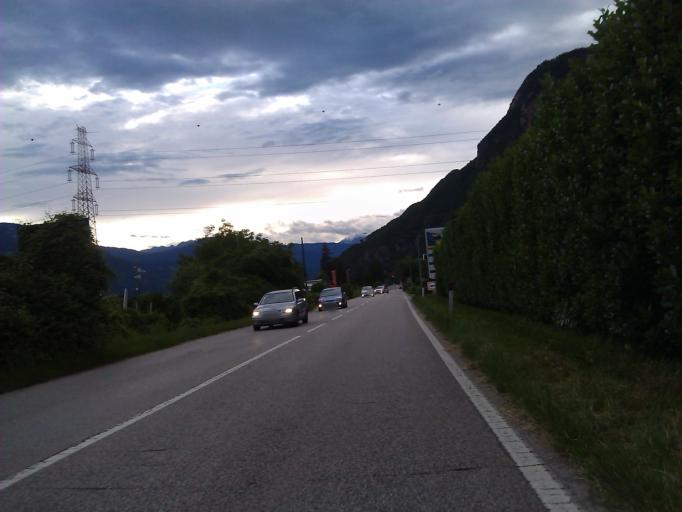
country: IT
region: Trentino-Alto Adige
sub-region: Bolzano
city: Bolzano
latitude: 46.4951
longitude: 11.3083
